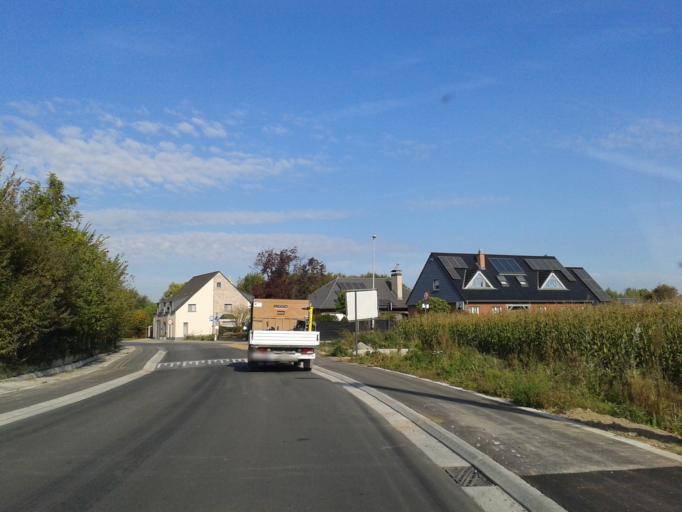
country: BE
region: Flanders
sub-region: Provincie Oost-Vlaanderen
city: Lebbeke
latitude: 50.9698
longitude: 4.1086
